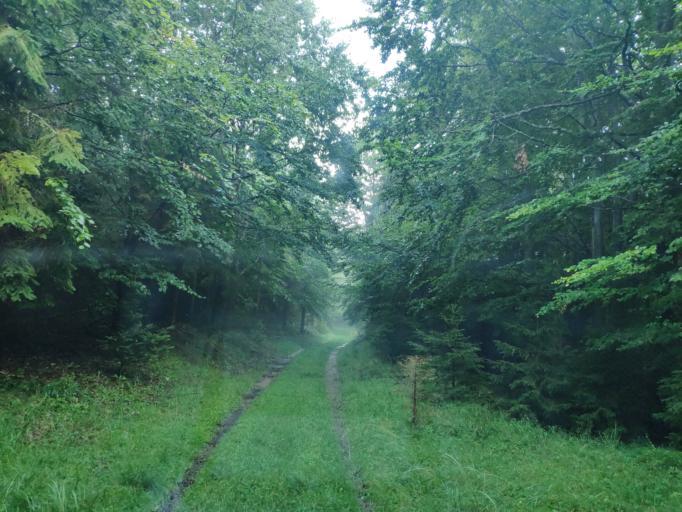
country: SK
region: Kosicky
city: Medzev
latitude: 48.7463
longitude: 20.9871
